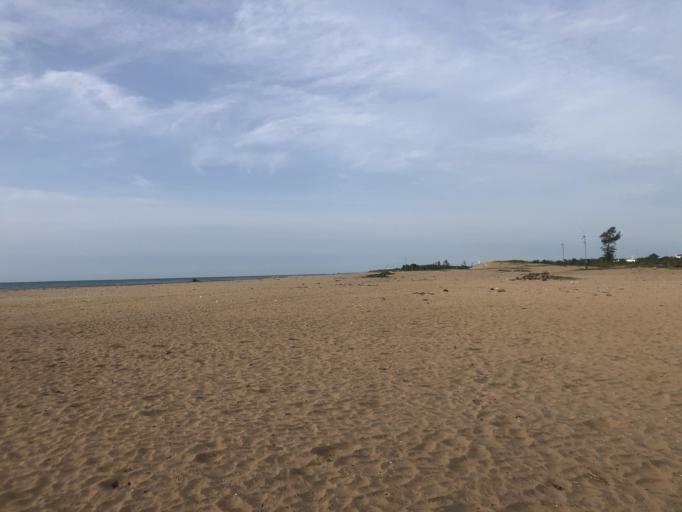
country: IN
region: Tamil Nadu
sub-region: Kancheepuram
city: Mamallapuram
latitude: 12.6144
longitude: 80.1980
